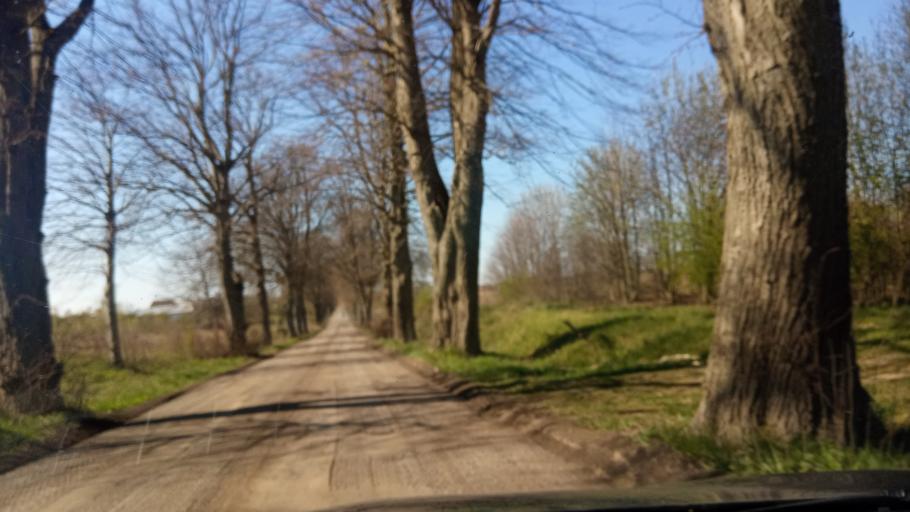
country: PL
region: West Pomeranian Voivodeship
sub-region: Powiat szczecinecki
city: Szczecinek
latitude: 53.6926
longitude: 16.7257
